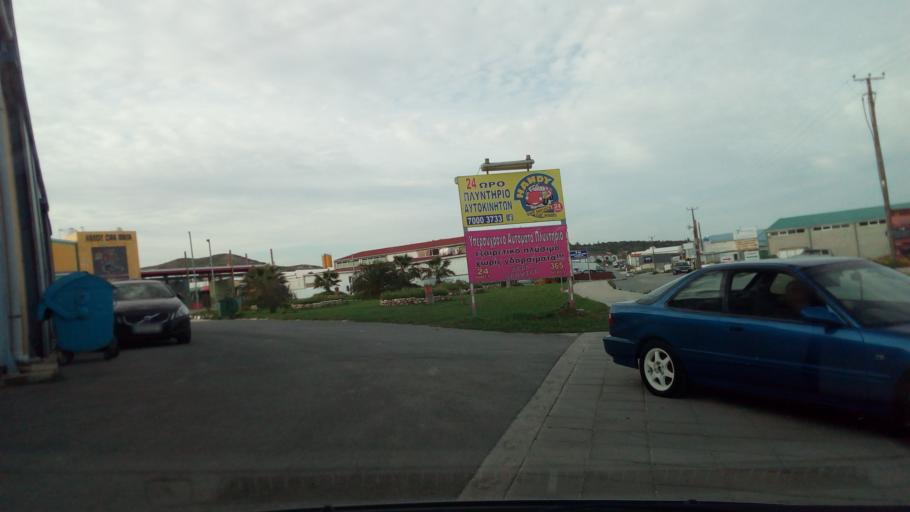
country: CY
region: Larnaka
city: Aradippou
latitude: 34.9291
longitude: 33.5757
